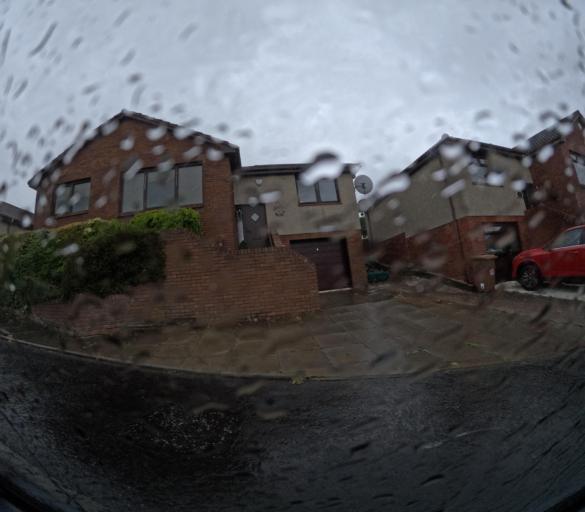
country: GB
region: Scotland
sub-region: West Lothian
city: West Calder
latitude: 55.8760
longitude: -3.5922
